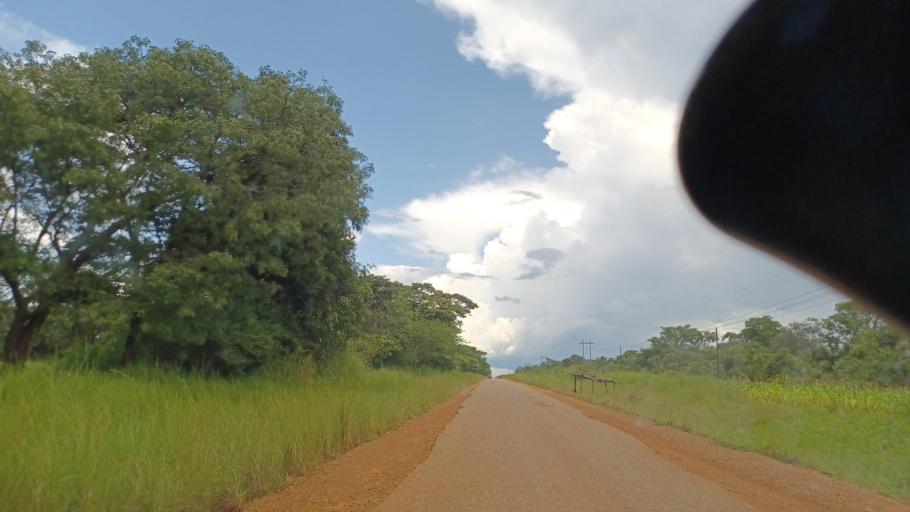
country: ZM
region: North-Western
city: Kasempa
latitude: -12.8706
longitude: 26.0407
